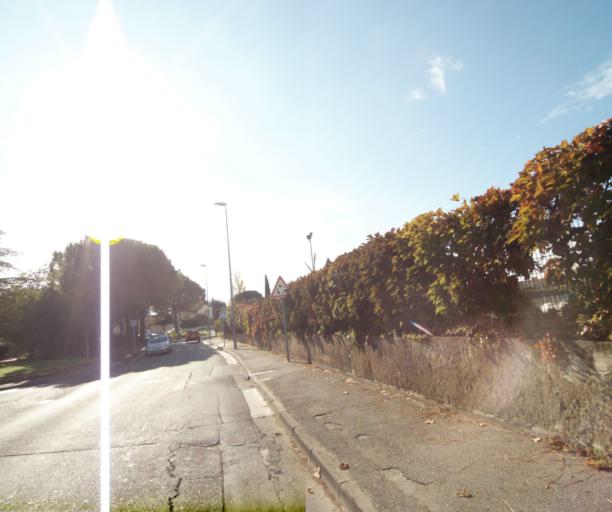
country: FR
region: Provence-Alpes-Cote d'Azur
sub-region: Departement des Bouches-du-Rhone
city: Plan-de-Cuques
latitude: 43.3483
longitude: 5.4680
